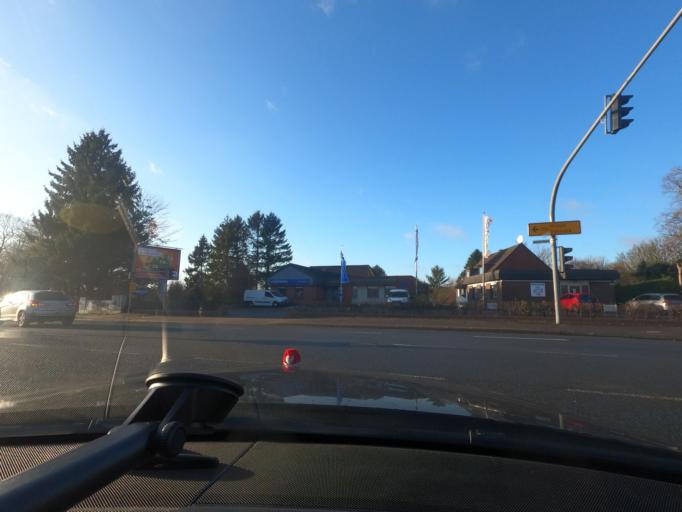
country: DE
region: Schleswig-Holstein
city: Flensburg
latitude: 54.7718
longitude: 9.4238
